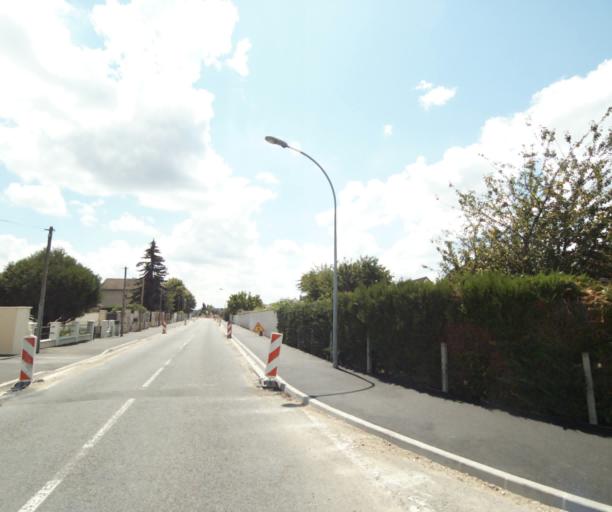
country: FR
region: Ile-de-France
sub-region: Departement de Seine-et-Marne
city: Hericy
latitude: 48.4410
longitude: 2.7565
